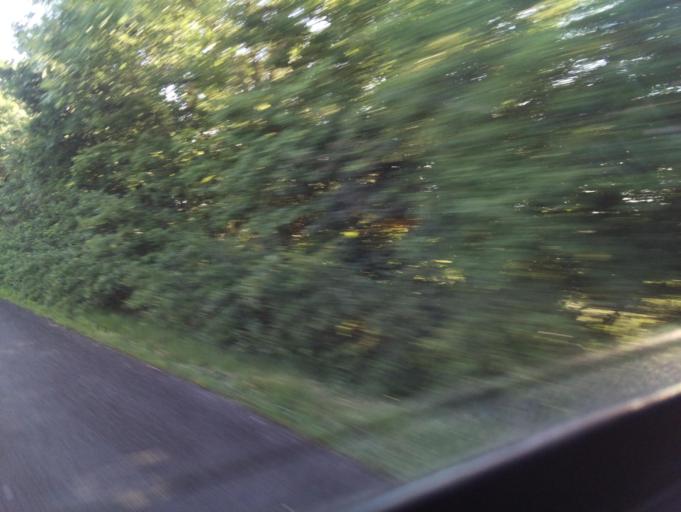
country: GB
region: England
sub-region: Lincolnshire
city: Navenby
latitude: 53.0964
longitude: -0.6160
